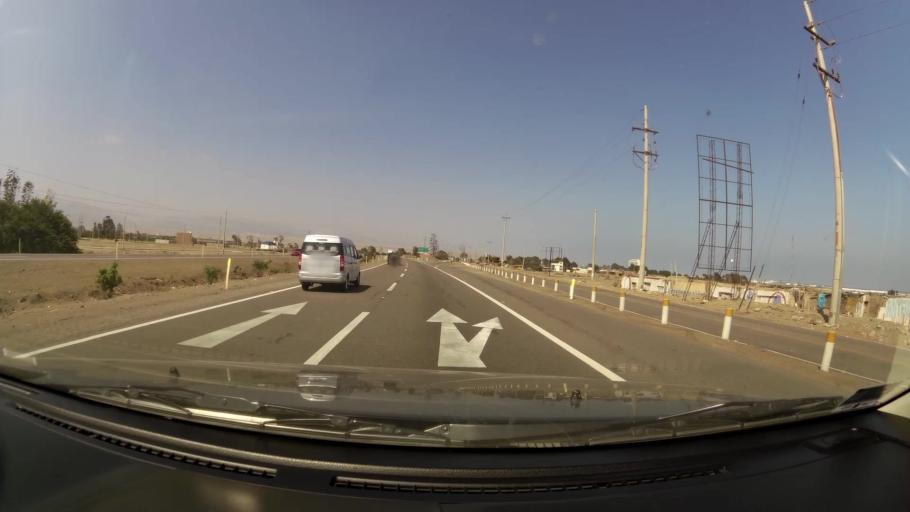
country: PE
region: Lima
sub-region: Provincia de Canete
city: Asia
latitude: -12.7785
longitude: -76.5858
